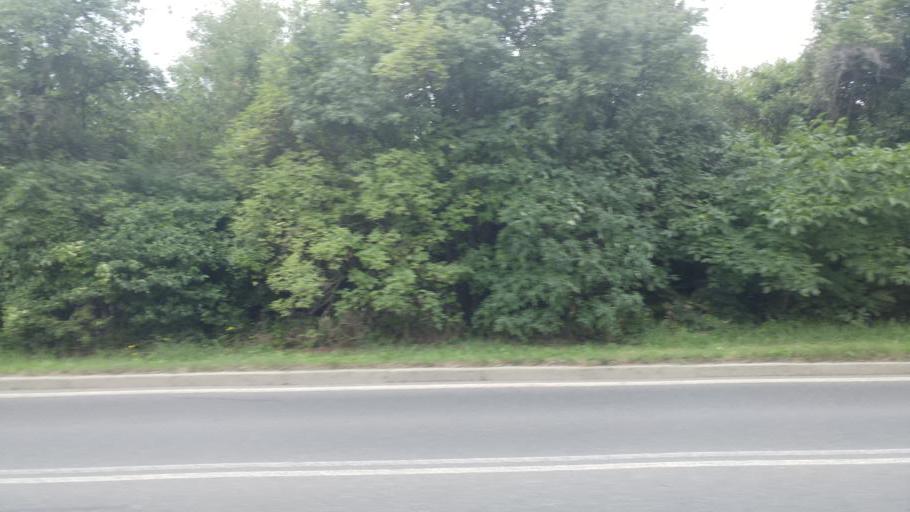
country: CZ
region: Central Bohemia
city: Roztoky
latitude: 50.1280
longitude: 14.3908
